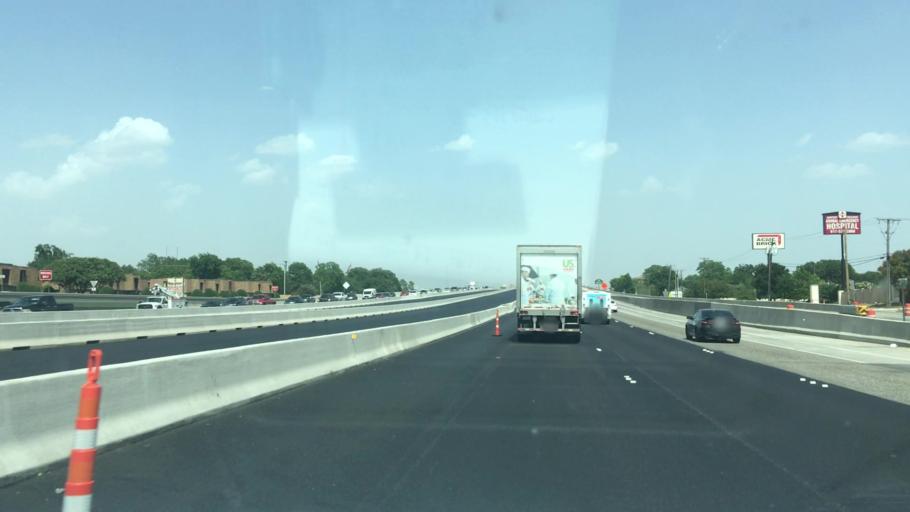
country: US
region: Texas
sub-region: Tarrant County
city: Euless
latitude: 32.8375
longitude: -97.0974
